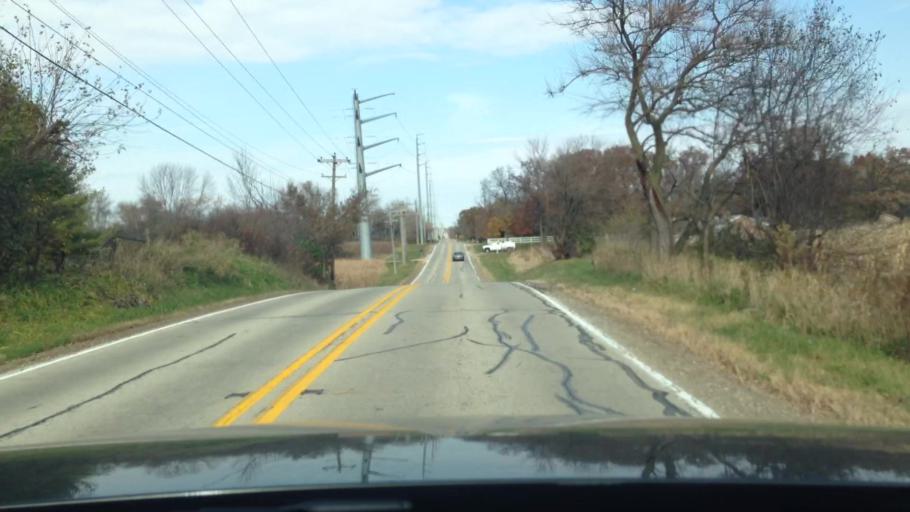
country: US
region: Illinois
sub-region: McHenry County
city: Woodstock
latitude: 42.2680
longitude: -88.4525
